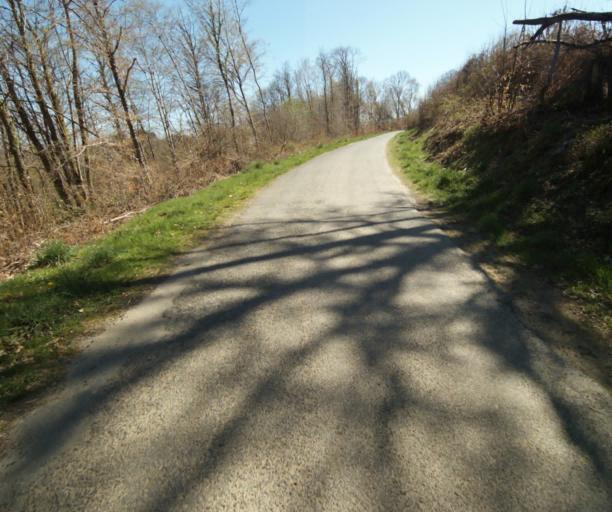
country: FR
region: Limousin
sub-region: Departement de la Correze
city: Chamboulive
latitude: 45.4428
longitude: 1.6819
